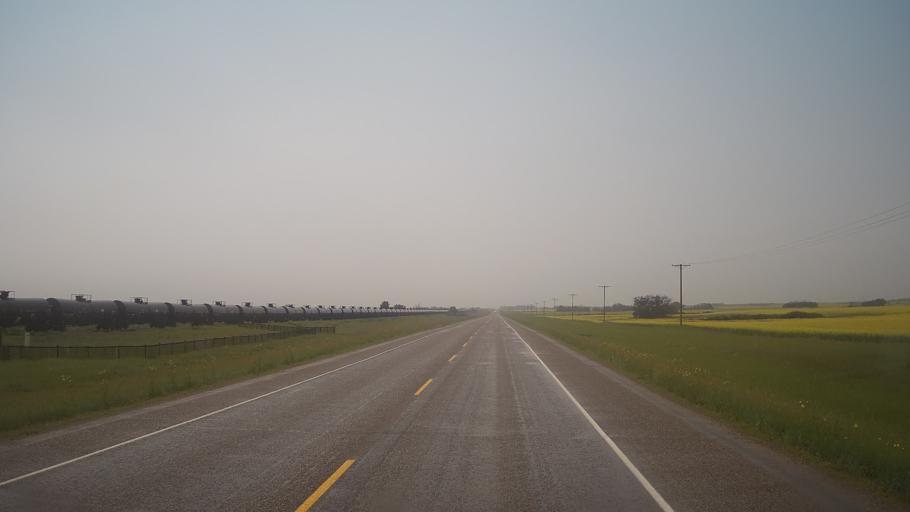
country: CA
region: Saskatchewan
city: Biggar
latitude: 52.1611
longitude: -108.2809
